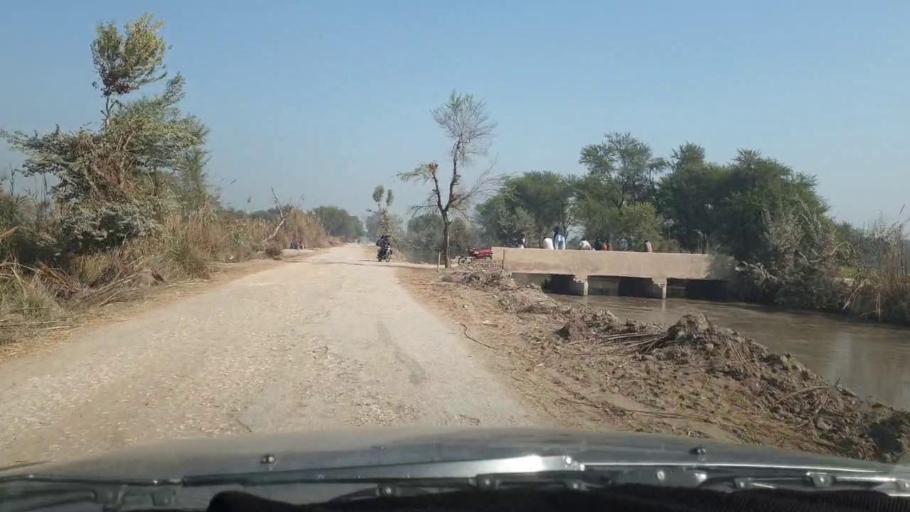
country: PK
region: Sindh
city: Khanpur
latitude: 27.7853
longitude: 69.5506
